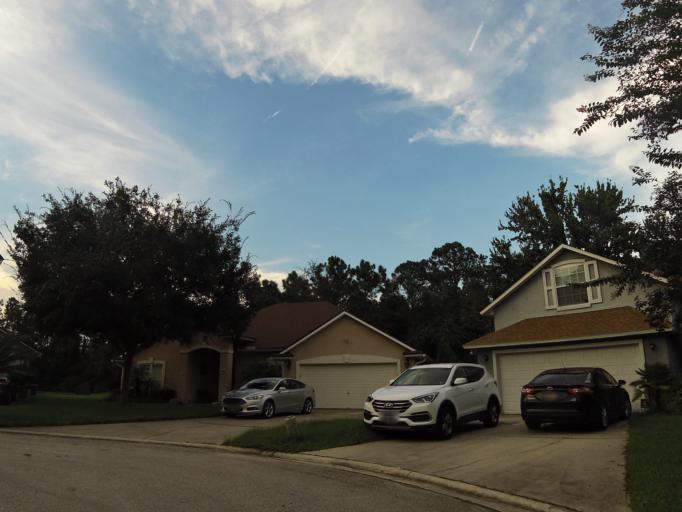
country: US
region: Florida
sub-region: Saint Johns County
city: Palm Valley
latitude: 30.2126
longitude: -81.5169
